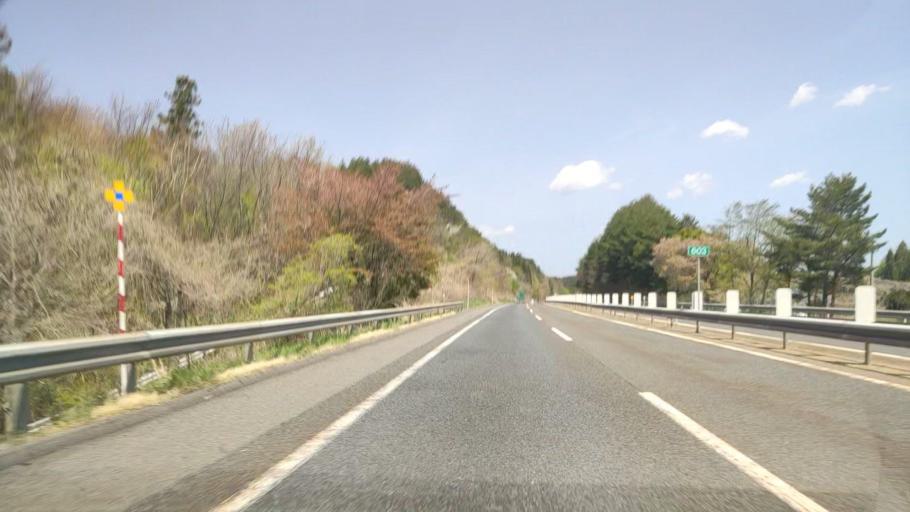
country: JP
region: Iwate
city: Ichinohe
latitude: 40.2654
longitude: 141.3997
